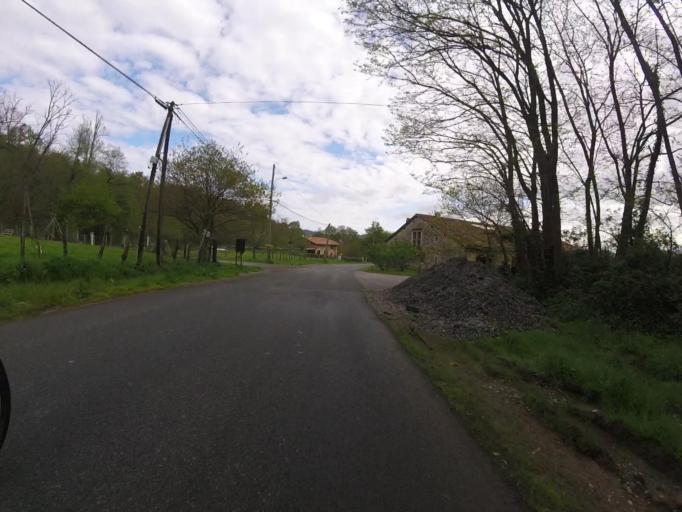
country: FR
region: Aquitaine
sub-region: Departement des Pyrenees-Atlantiques
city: Sare
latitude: 43.3044
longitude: -1.5926
